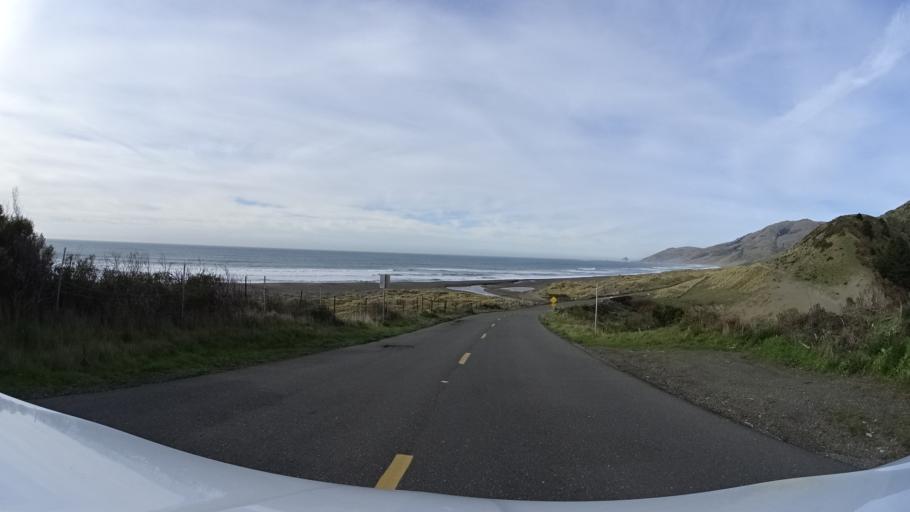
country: US
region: California
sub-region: Humboldt County
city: Ferndale
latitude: 40.3510
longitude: -124.3596
